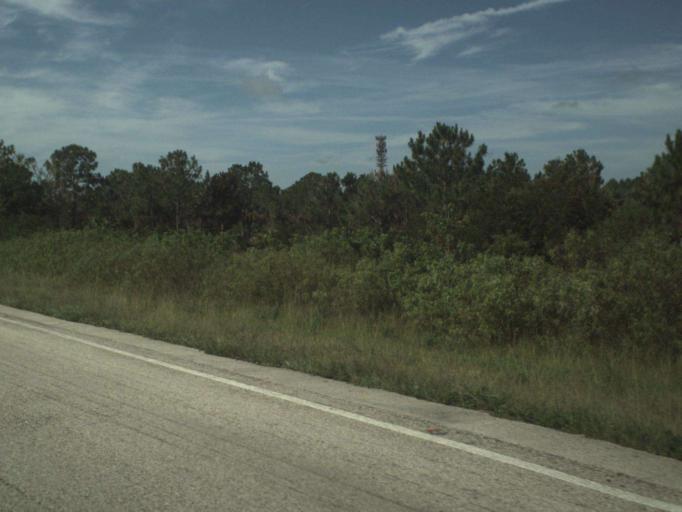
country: US
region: Florida
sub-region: Indian River County
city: Fellsmere
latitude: 27.7716
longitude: -80.5511
